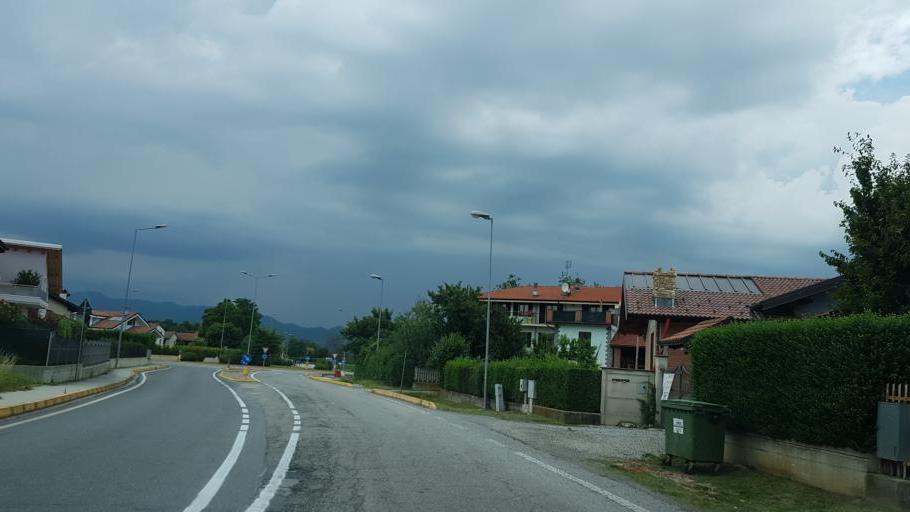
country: IT
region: Piedmont
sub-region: Provincia di Cuneo
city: Cervasca
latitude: 44.3846
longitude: 7.4664
